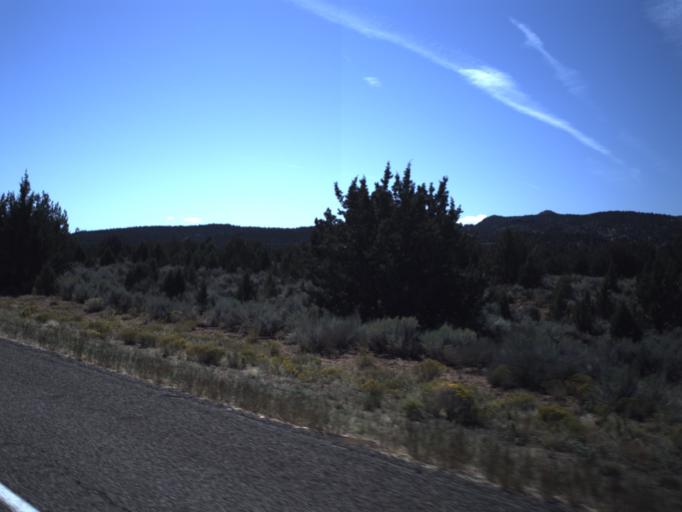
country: US
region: Utah
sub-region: Washington County
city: Ivins
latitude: 37.2950
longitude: -113.6631
